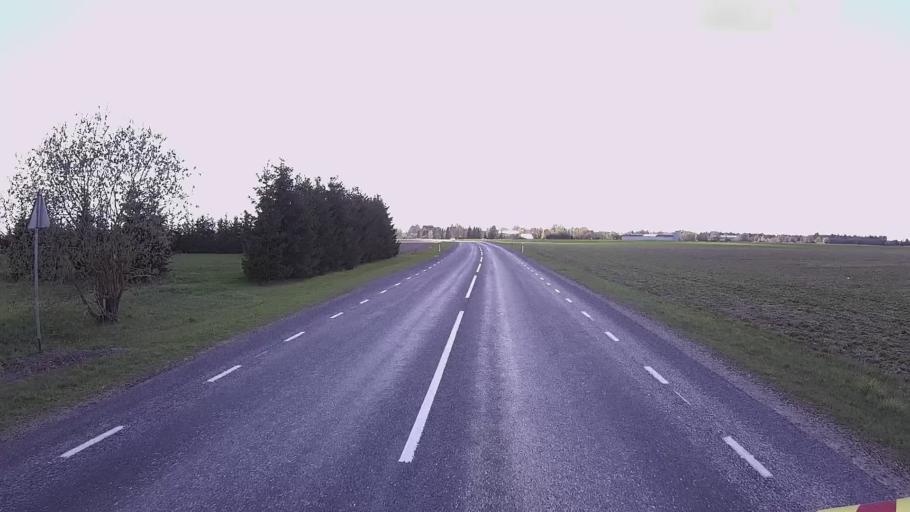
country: EE
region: Jogevamaa
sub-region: Jogeva linn
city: Jogeva
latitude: 58.7332
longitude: 26.2129
